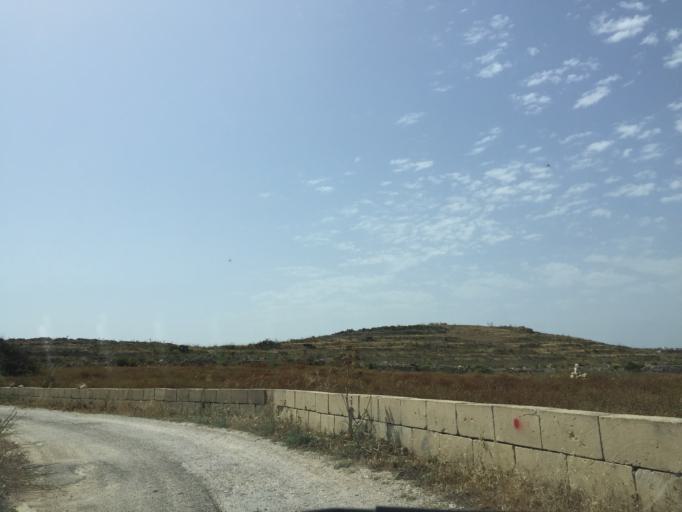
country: MT
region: In-Nadur
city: Nadur
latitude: 36.0621
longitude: 14.2895
